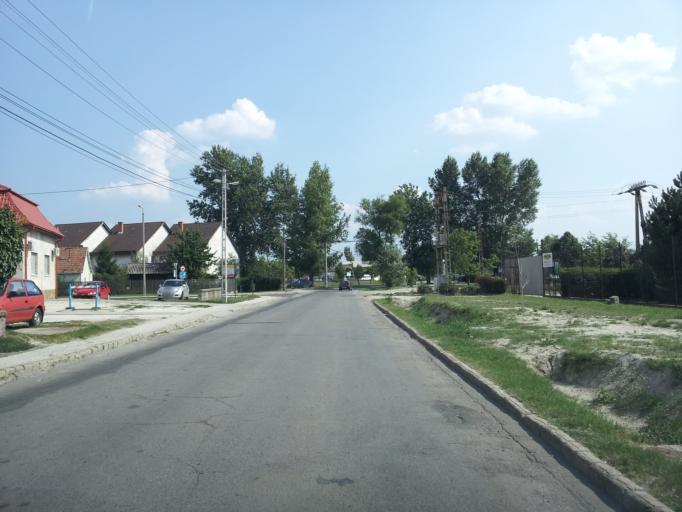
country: HU
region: Pest
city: Szigetszentmiklos
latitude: 47.3391
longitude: 19.0296
